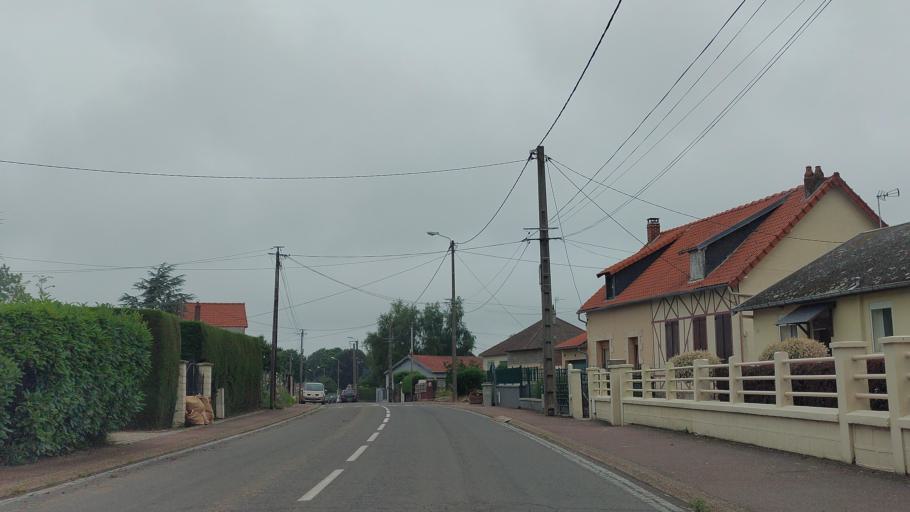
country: FR
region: Picardie
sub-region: Departement de la Somme
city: Bethencourt-sur-Mer
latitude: 50.0817
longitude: 1.4977
